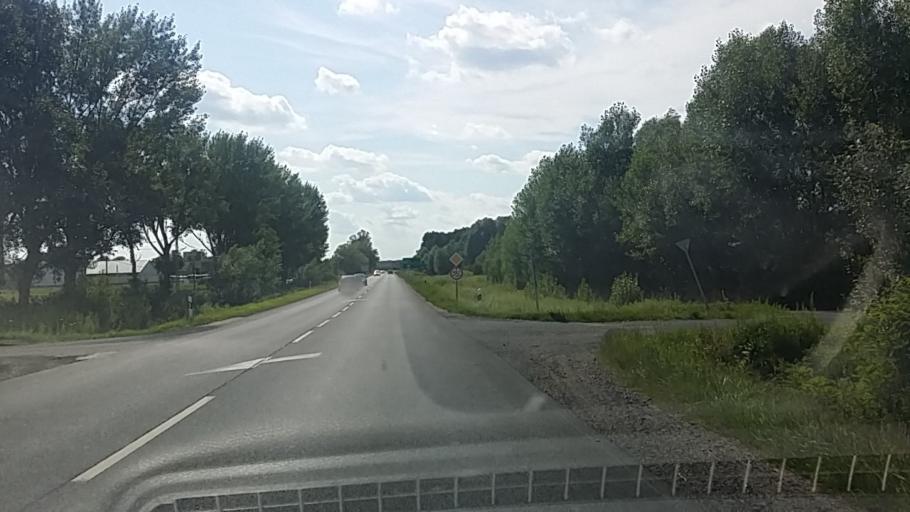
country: HU
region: Zala
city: Nagykanizsa
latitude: 46.4670
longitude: 16.9766
